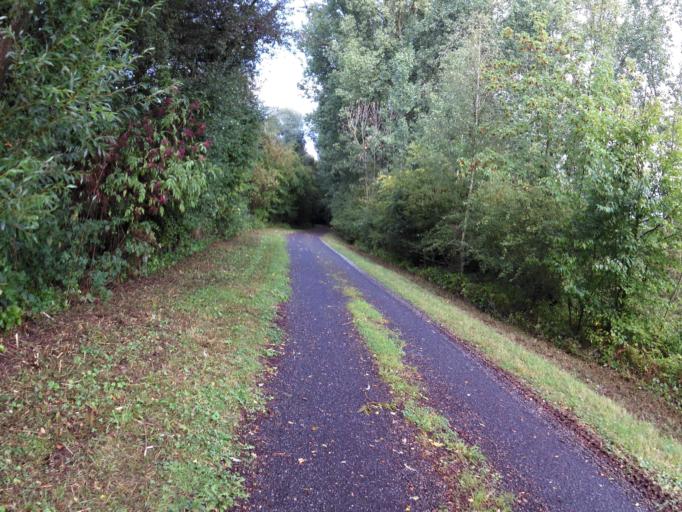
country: DE
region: Lower Saxony
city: Nienburg
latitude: 52.6528
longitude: 9.2036
